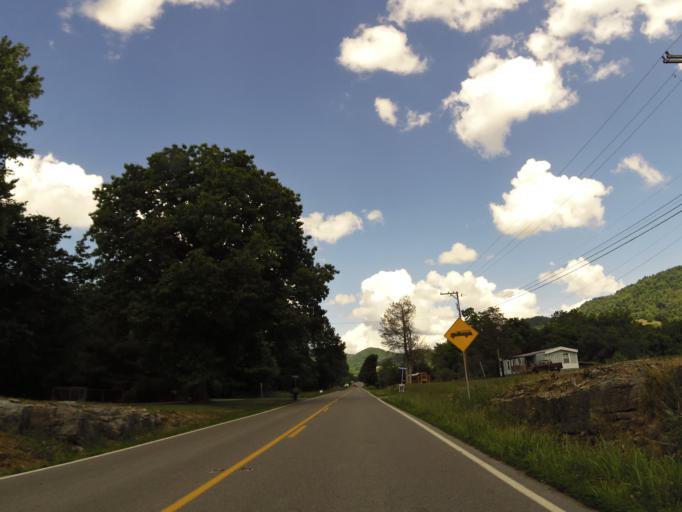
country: US
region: Virginia
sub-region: Lee County
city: Dryden
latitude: 36.7069
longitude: -82.9699
